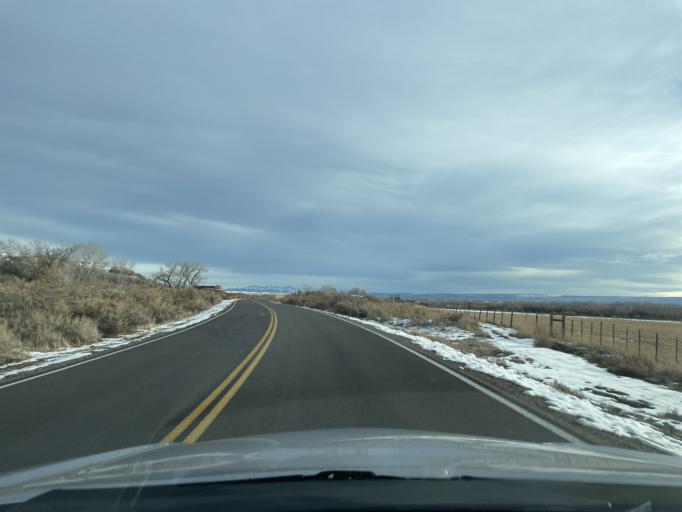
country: US
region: Colorado
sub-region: Montrose County
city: Olathe
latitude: 38.6649
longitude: -107.9994
